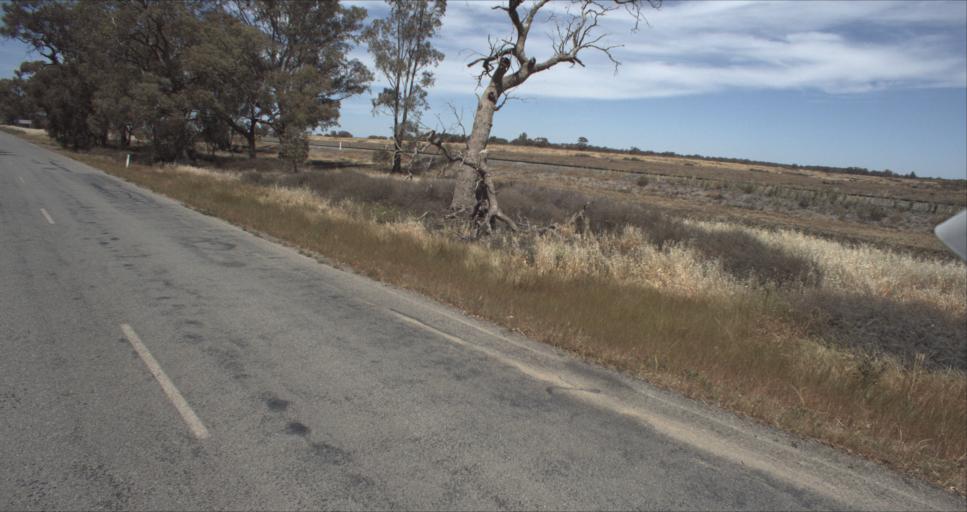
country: AU
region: New South Wales
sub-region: Leeton
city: Leeton
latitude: -34.6415
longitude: 146.4671
